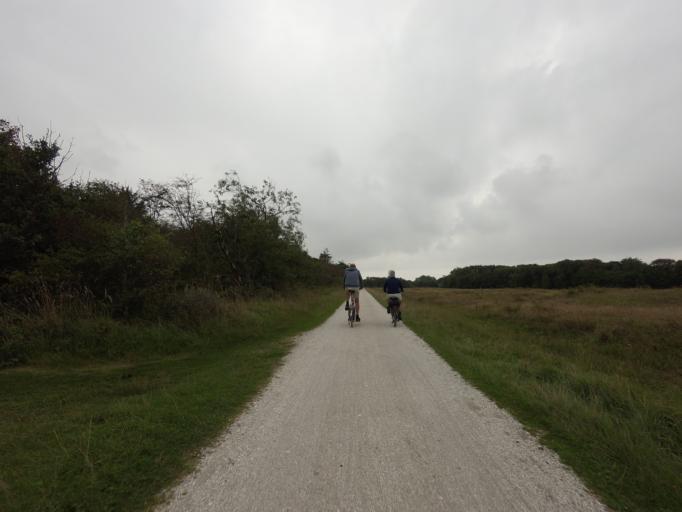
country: NL
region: Friesland
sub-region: Gemeente Schiermonnikoog
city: Schiermonnikoog
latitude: 53.4884
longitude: 6.1622
